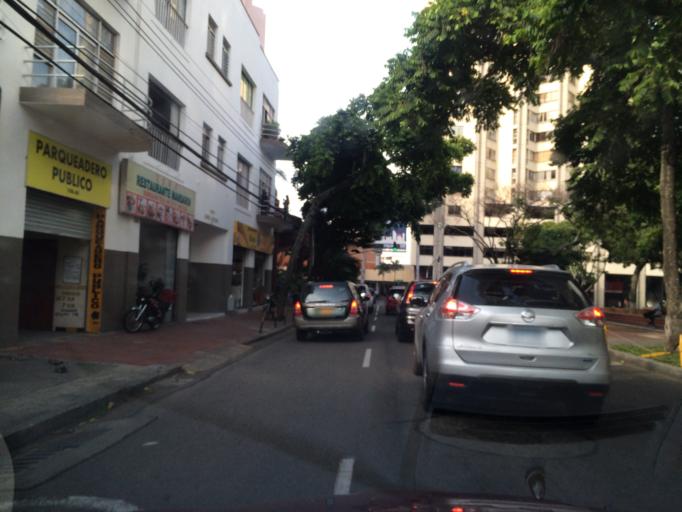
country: CO
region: Valle del Cauca
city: Cali
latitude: 3.4556
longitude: -76.5345
